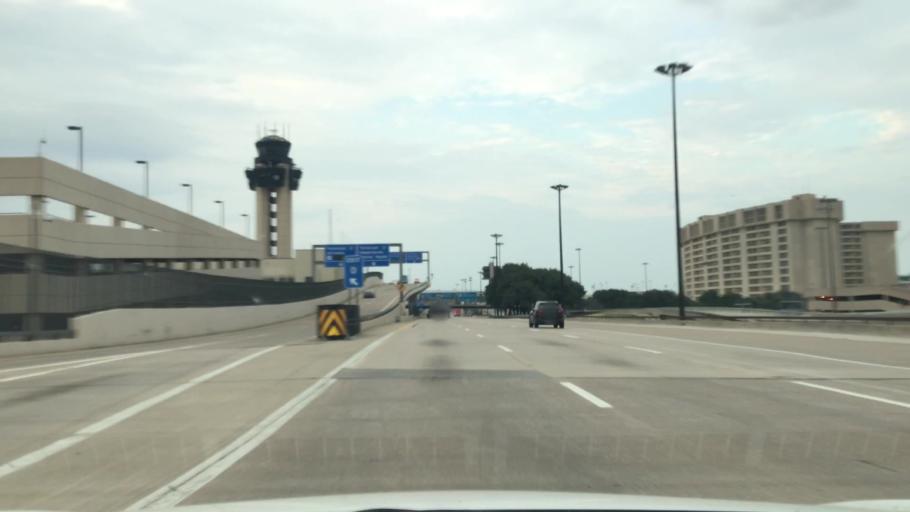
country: US
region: Texas
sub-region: Tarrant County
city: Grapevine
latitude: 32.8944
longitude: -97.0399
